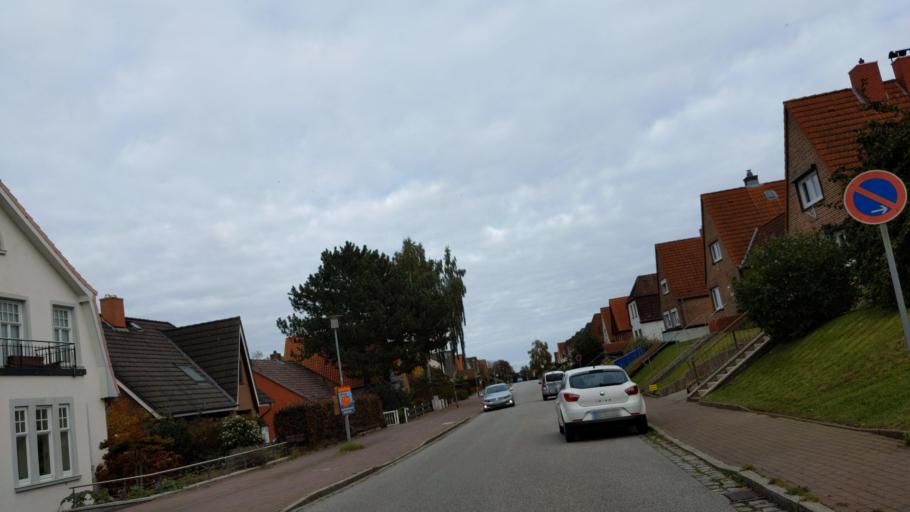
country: DE
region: Schleswig-Holstein
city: Neustadt in Holstein
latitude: 54.1127
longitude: 10.8206
